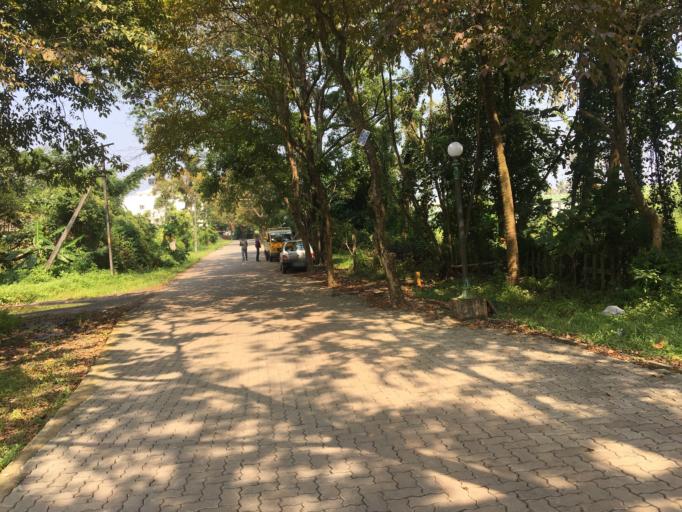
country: IN
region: Kerala
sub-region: Ernakulam
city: Cochin
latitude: 9.9619
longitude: 76.3226
